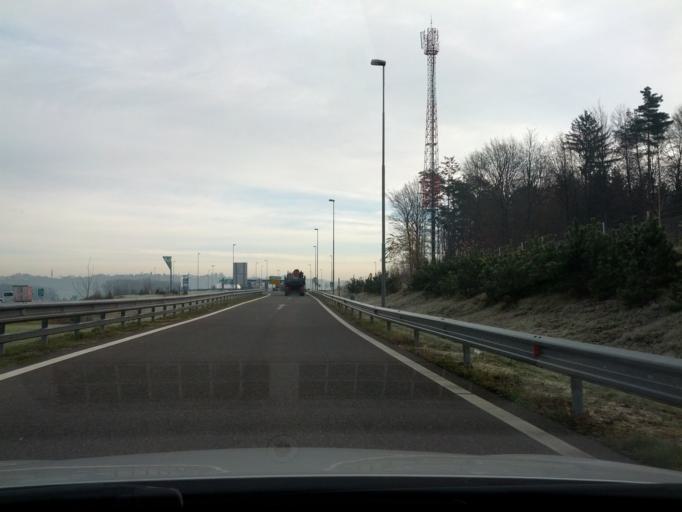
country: SI
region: Sveti Jurij
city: Sveti Jurij ob Scavnici
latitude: 46.5827
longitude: 16.0046
